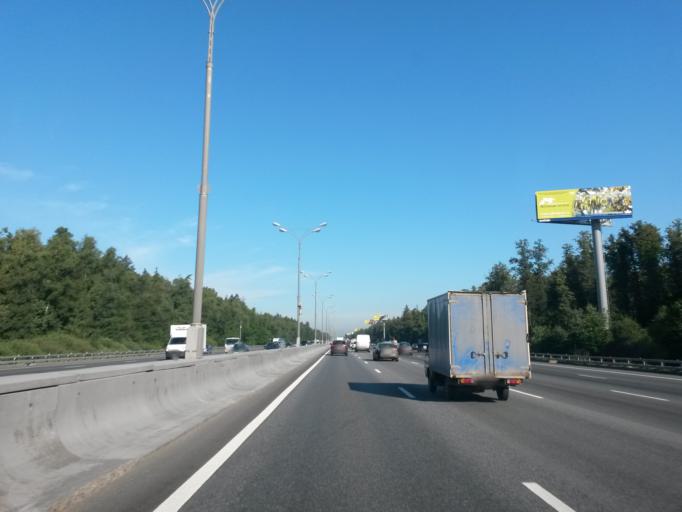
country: RU
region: Moscow
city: Gol'yanovo
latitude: 55.8414
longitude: 37.8058
